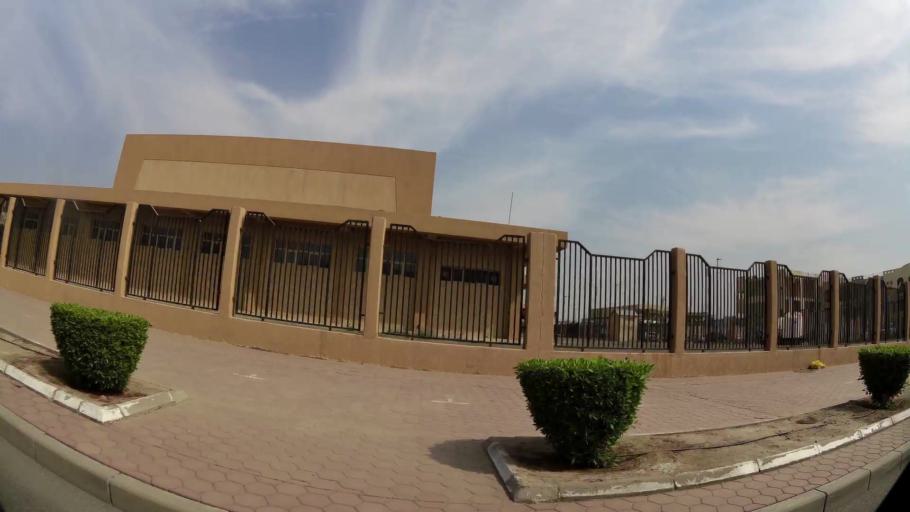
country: KW
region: Al Asimah
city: Ash Shamiyah
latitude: 29.3387
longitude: 47.9765
